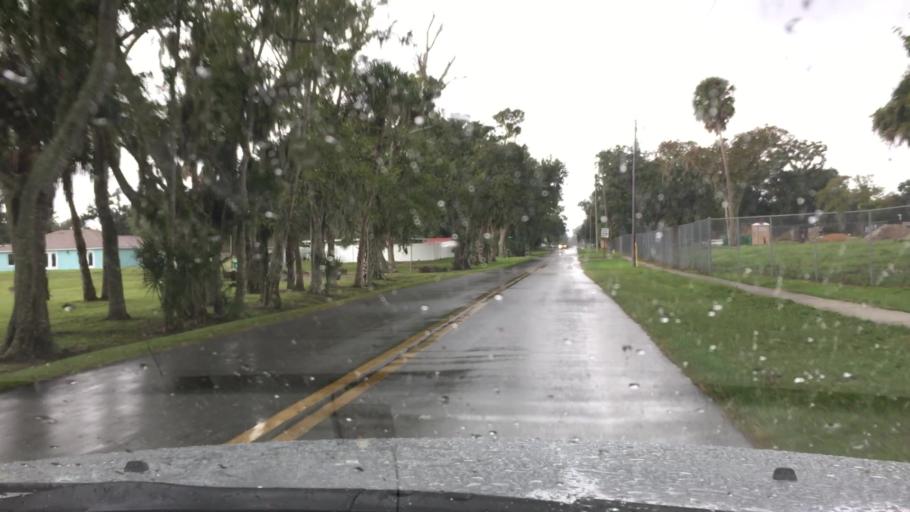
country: US
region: Florida
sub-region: Volusia County
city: Holly Hill
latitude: 29.2410
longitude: -81.0437
